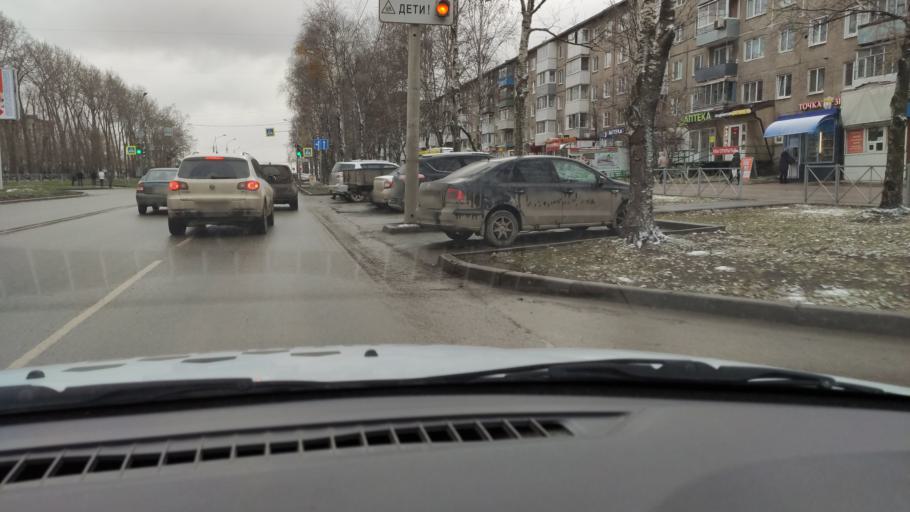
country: RU
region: Perm
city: Kondratovo
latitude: 57.9639
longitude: 56.1781
